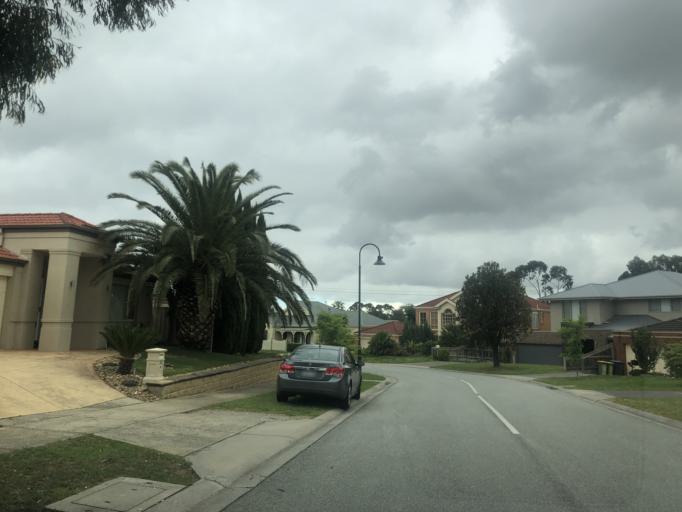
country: AU
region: Victoria
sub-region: Knox
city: Rowville
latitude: -37.9382
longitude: 145.2500
